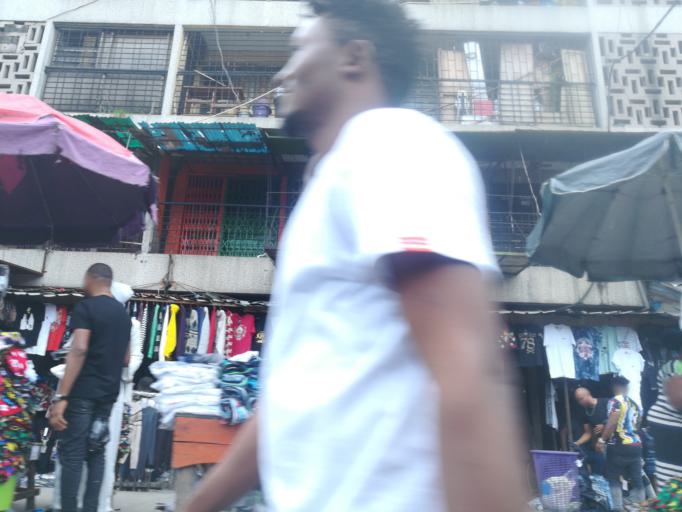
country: NG
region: Lagos
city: Lagos
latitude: 6.4560
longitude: 3.3866
